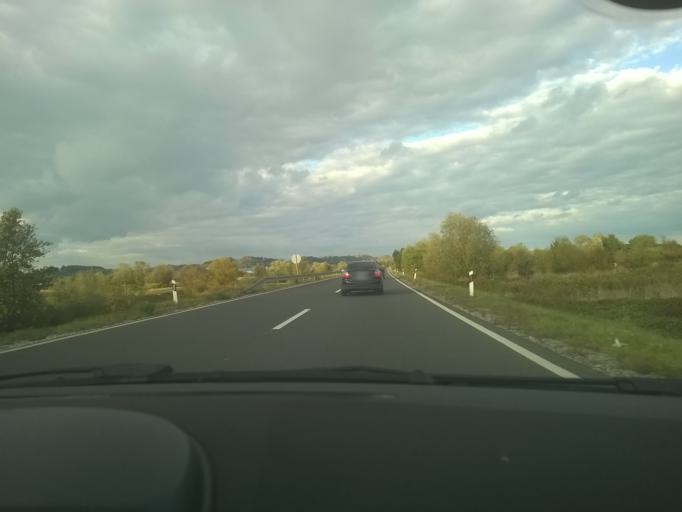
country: HR
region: Zagrebacka
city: Jakovlje
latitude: 45.9406
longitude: 15.8223
